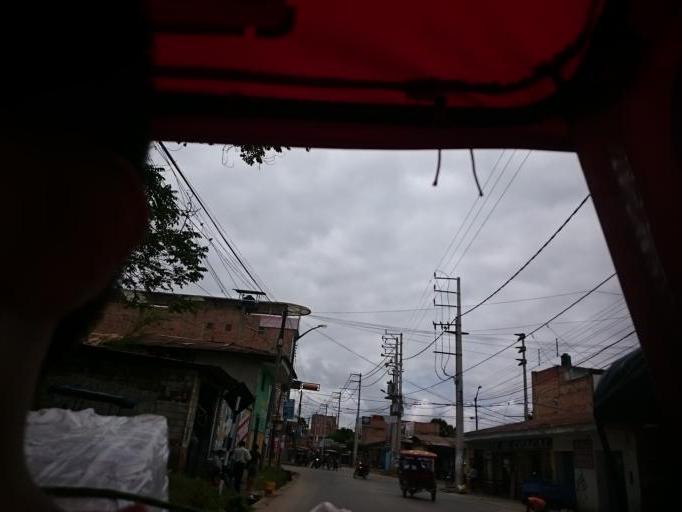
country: PE
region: San Martin
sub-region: Provincia de San Martin
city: Tarapoto
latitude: -6.4916
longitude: -76.3639
